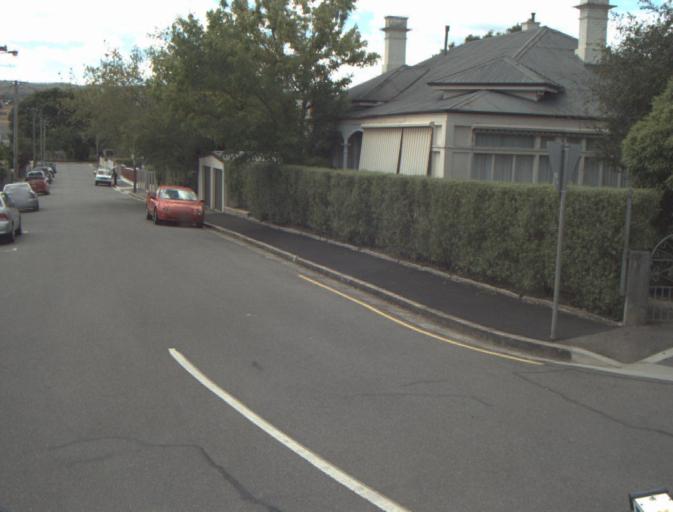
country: AU
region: Tasmania
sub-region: Launceston
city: East Launceston
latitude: -41.4346
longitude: 147.1545
